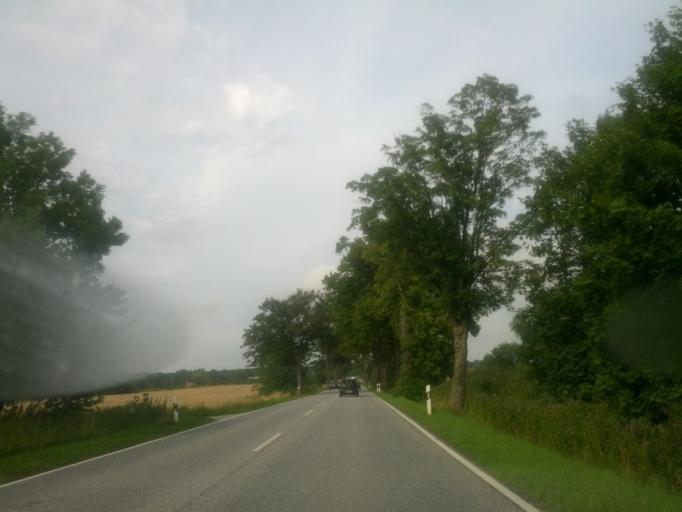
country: DE
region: Mecklenburg-Vorpommern
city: Neubukow
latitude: 53.9869
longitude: 11.6300
